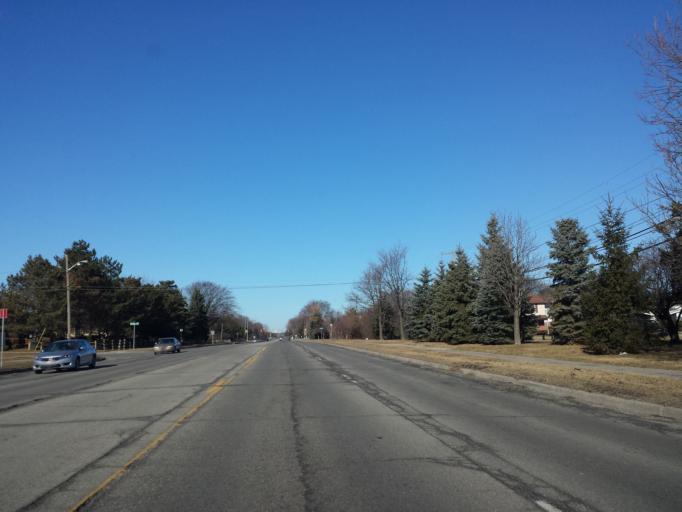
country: US
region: Michigan
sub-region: Oakland County
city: Lathrup Village
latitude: 42.5018
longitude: -83.2478
